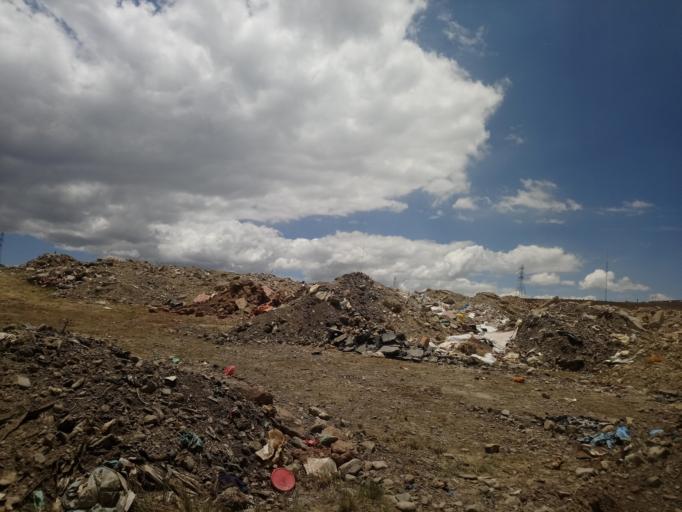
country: BO
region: La Paz
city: La Paz
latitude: -16.4381
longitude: -68.1630
